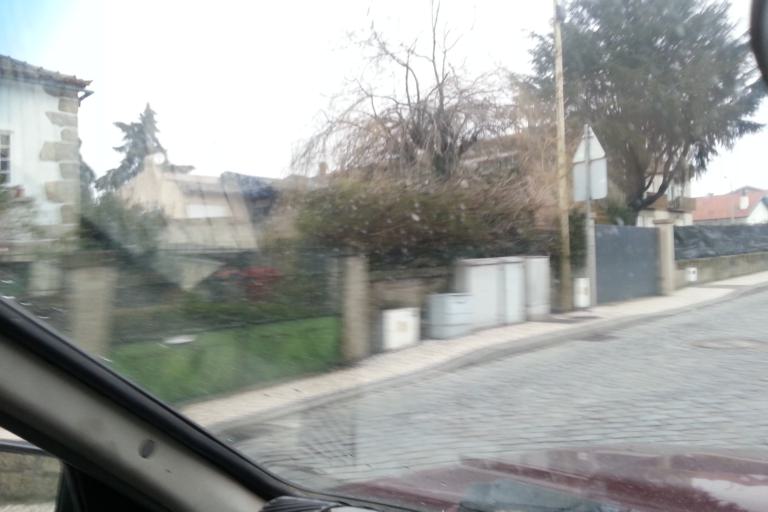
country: PT
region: Viseu
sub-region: Mangualde
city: Mangualde
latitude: 40.6046
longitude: -7.7508
